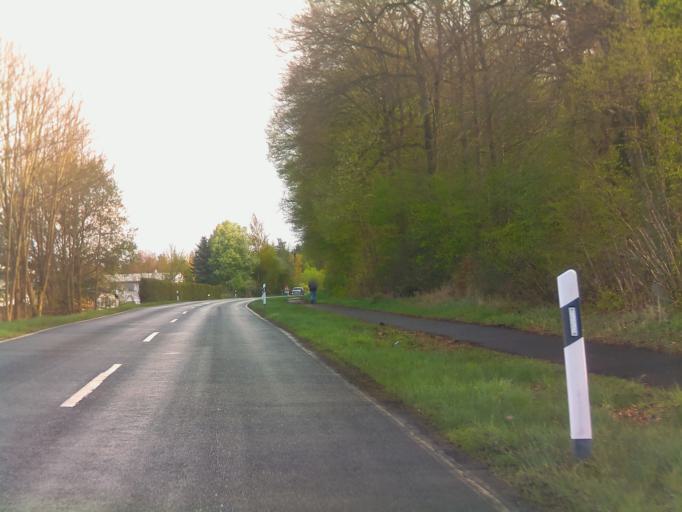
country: DE
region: Hesse
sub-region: Regierungsbezirk Giessen
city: Wetzlar
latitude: 50.5347
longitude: 8.5307
